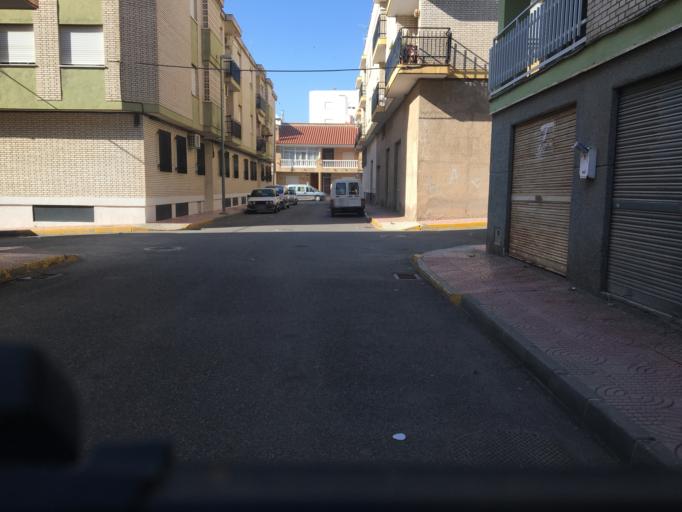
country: ES
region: Murcia
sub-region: Murcia
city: Puerto Lumbreras
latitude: 37.5586
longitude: -1.8101
